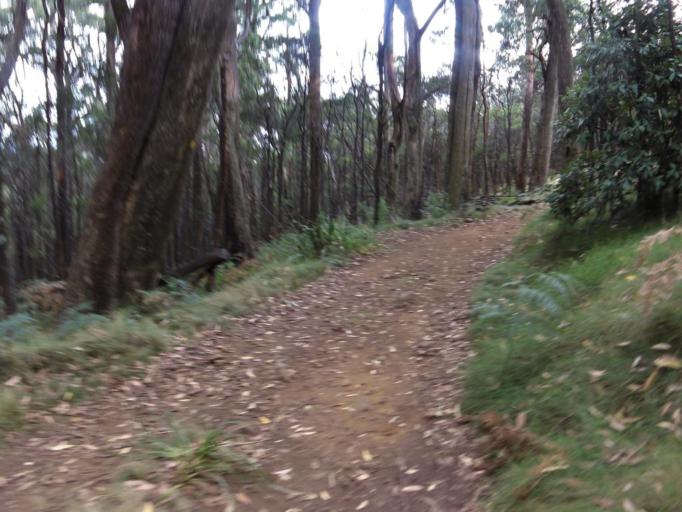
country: AU
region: Victoria
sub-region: Hume
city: Sunbury
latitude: -37.3850
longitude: 144.5741
